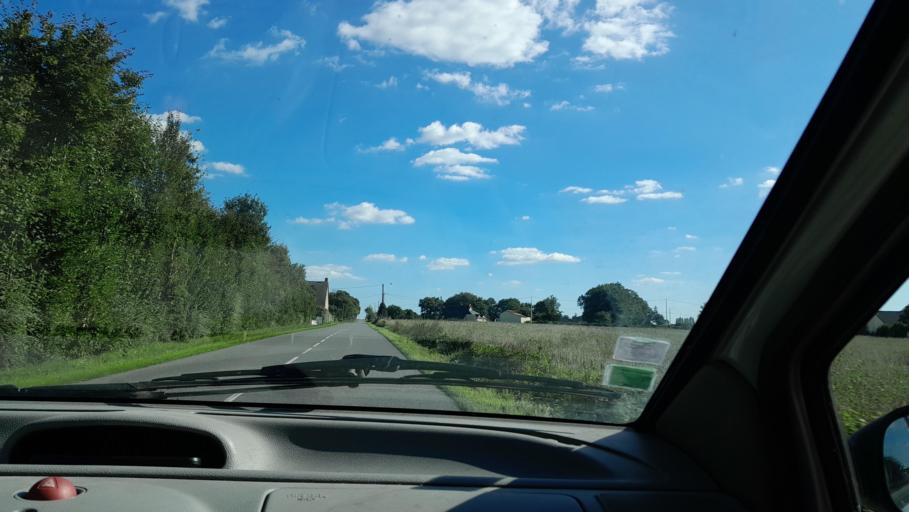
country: FR
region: Pays de la Loire
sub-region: Departement de la Mayenne
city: Ballots
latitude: 47.9629
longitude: -1.1139
